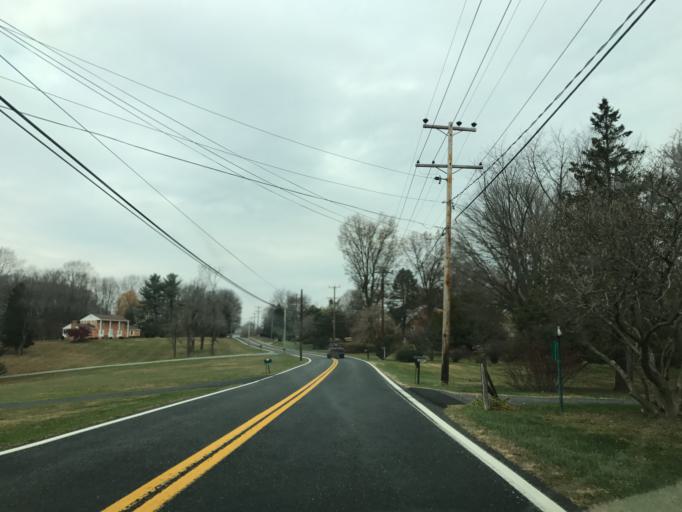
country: US
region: Maryland
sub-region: Baltimore County
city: Hampton
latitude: 39.4844
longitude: -76.5204
